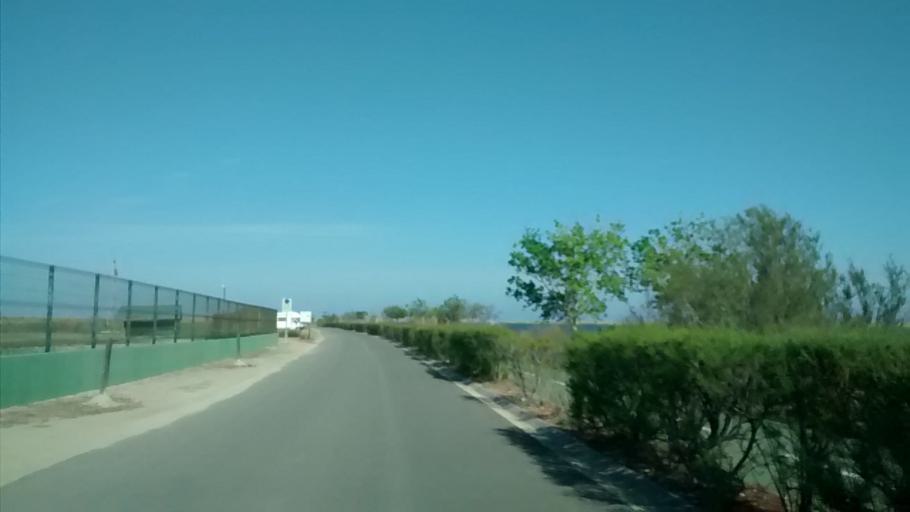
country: ES
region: Catalonia
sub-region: Provincia de Tarragona
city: Deltebre
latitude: 40.7192
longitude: 0.8523
